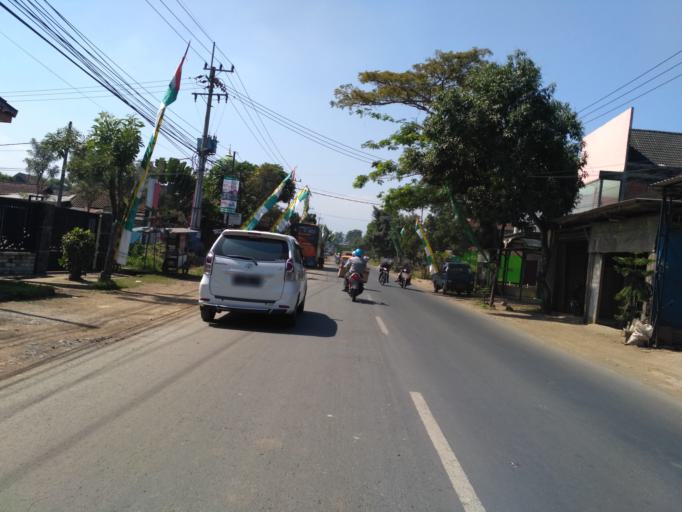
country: ID
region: East Java
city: Tamiajeng
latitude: -7.9534
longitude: 112.6972
